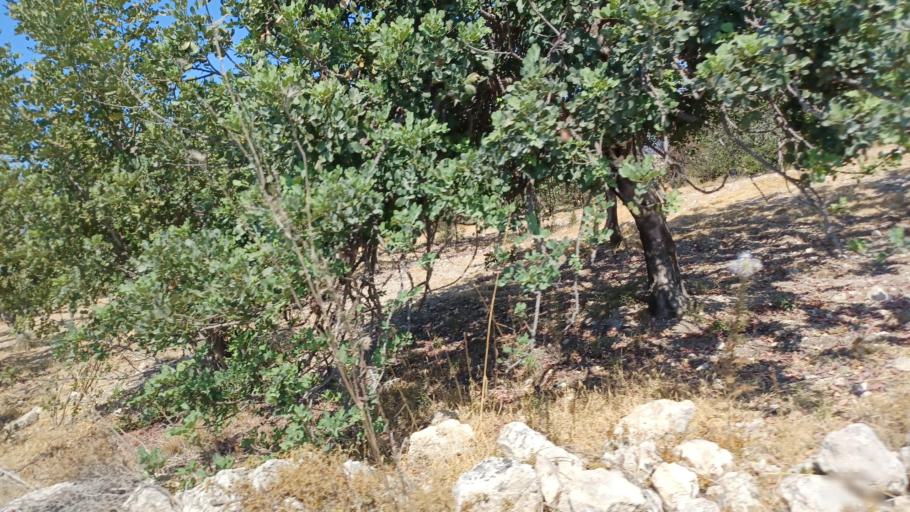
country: CY
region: Pafos
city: Polis
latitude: 34.9680
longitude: 32.4916
